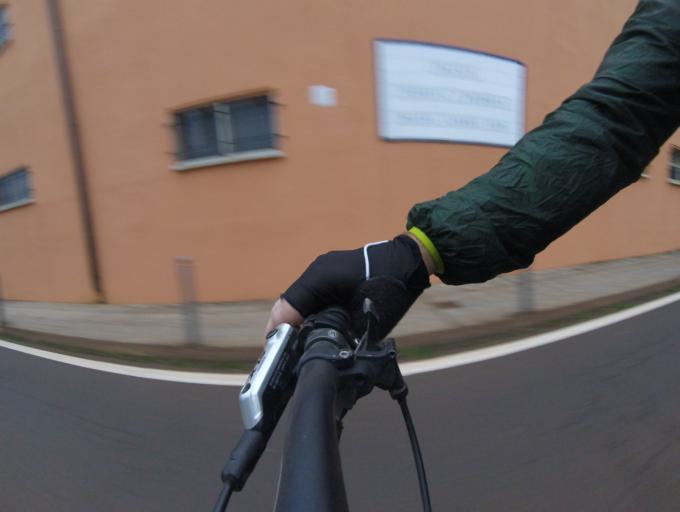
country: ES
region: Canary Islands
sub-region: Provincia de Santa Cruz de Tenerife
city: La Laguna
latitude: 28.4406
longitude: -16.3354
